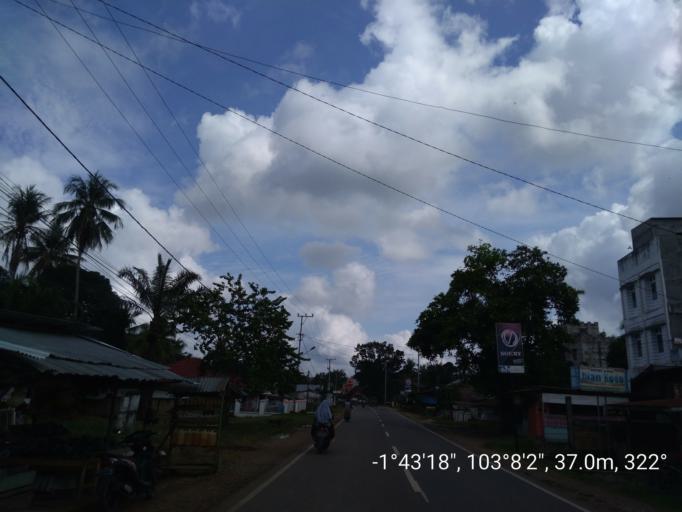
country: ID
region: Jambi
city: Muara Tembesi
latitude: -1.7218
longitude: 103.1342
